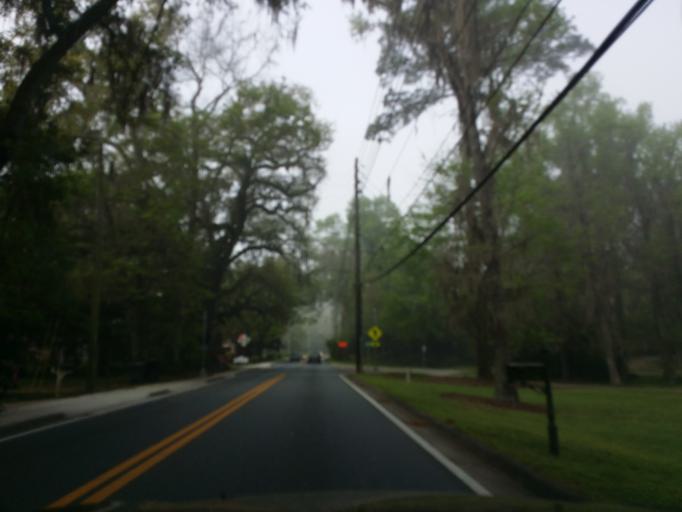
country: US
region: Florida
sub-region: Leon County
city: Tallahassee
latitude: 30.4681
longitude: -84.2514
